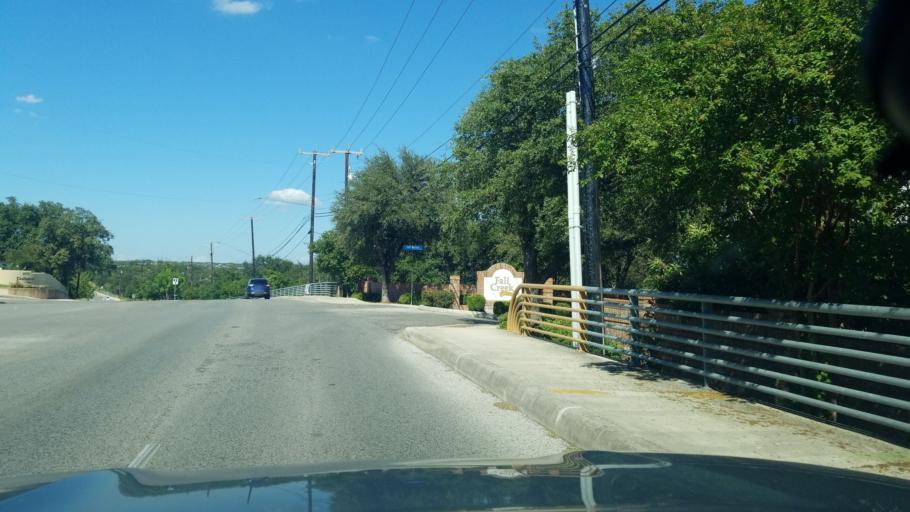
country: US
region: Texas
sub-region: Bexar County
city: Hollywood Park
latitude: 29.5817
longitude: -98.4388
